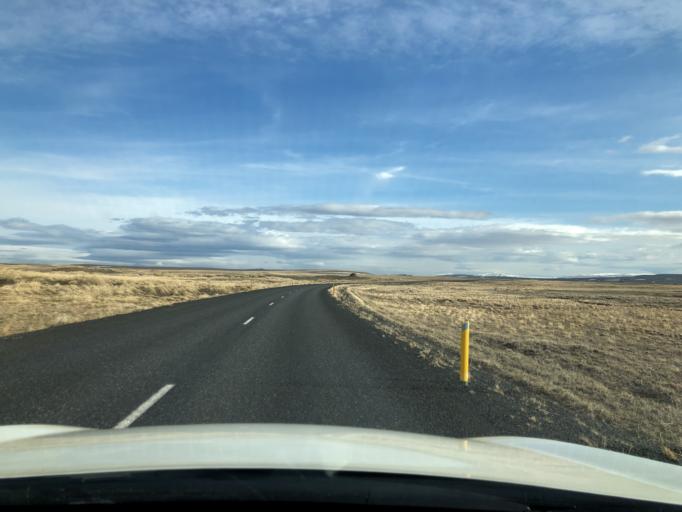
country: IS
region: Northeast
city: Laugar
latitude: 65.7366
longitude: -16.4001
